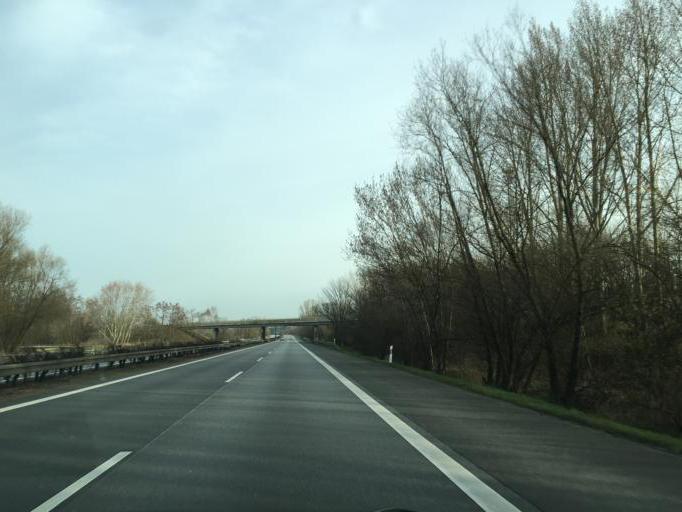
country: DE
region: Berlin
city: Blankenfelde
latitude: 52.6603
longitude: 13.4106
